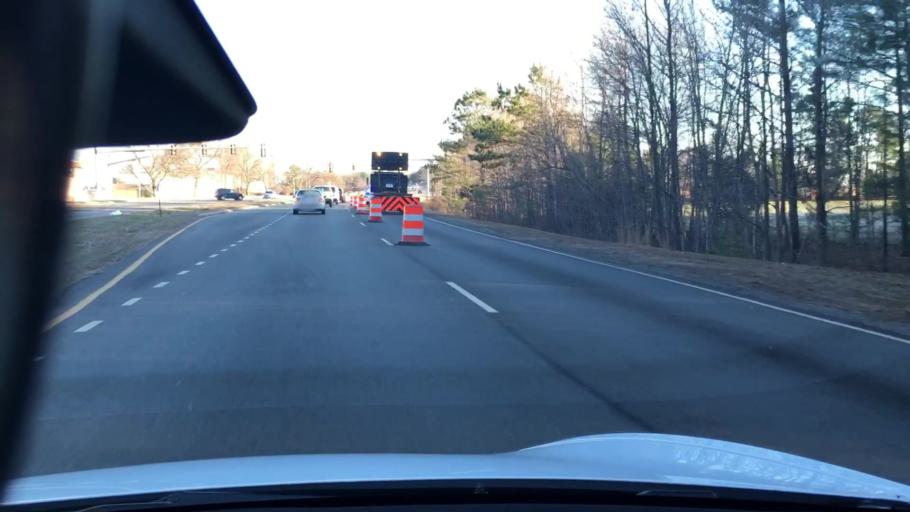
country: US
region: Virginia
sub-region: Henrico County
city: Fort Lee
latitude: 37.4920
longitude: -77.3533
